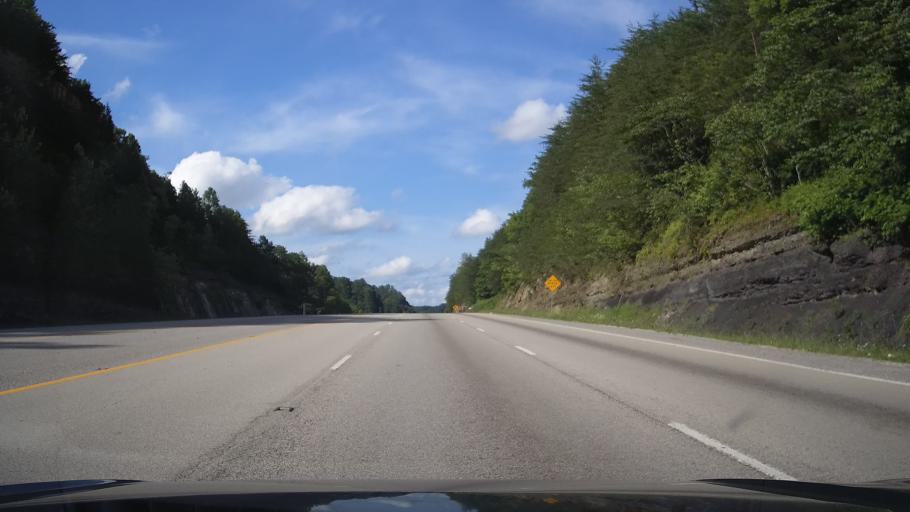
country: US
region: Kentucky
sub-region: Lawrence County
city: Louisa
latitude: 38.0357
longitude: -82.6511
